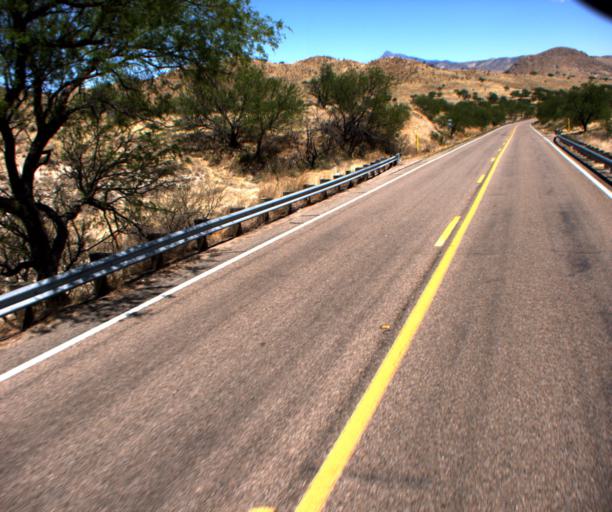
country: US
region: Arizona
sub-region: Santa Cruz County
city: Rio Rico
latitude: 31.4726
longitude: -110.8204
